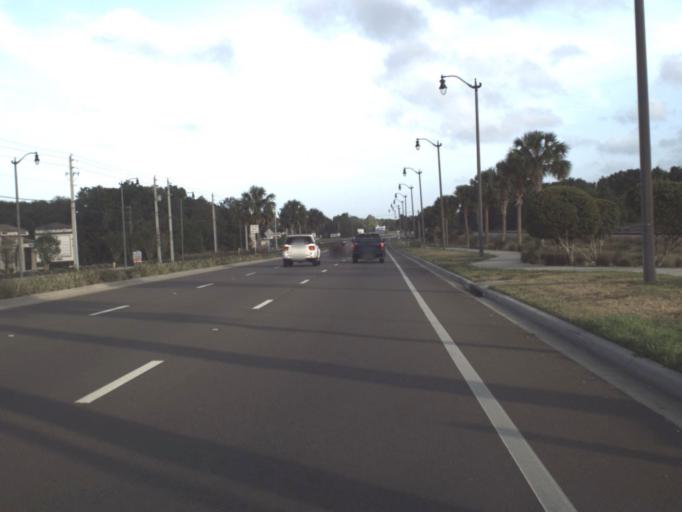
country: US
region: Florida
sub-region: Brevard County
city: Rockledge
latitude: 28.3243
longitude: -80.7173
